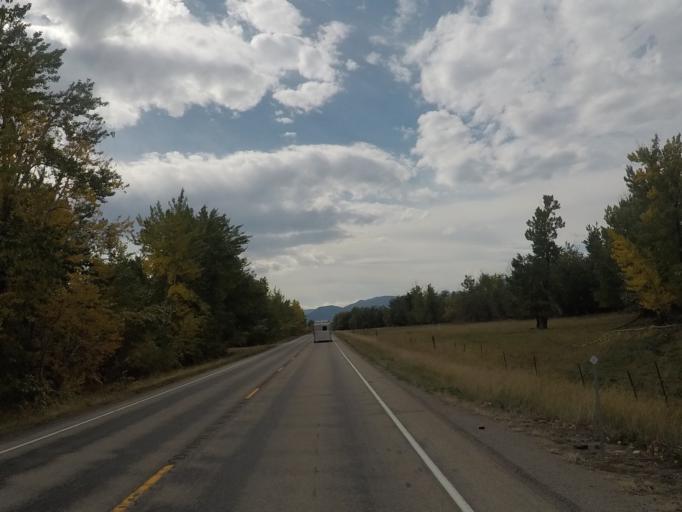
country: US
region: Montana
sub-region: Carbon County
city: Red Lodge
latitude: 45.2745
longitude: -109.2190
